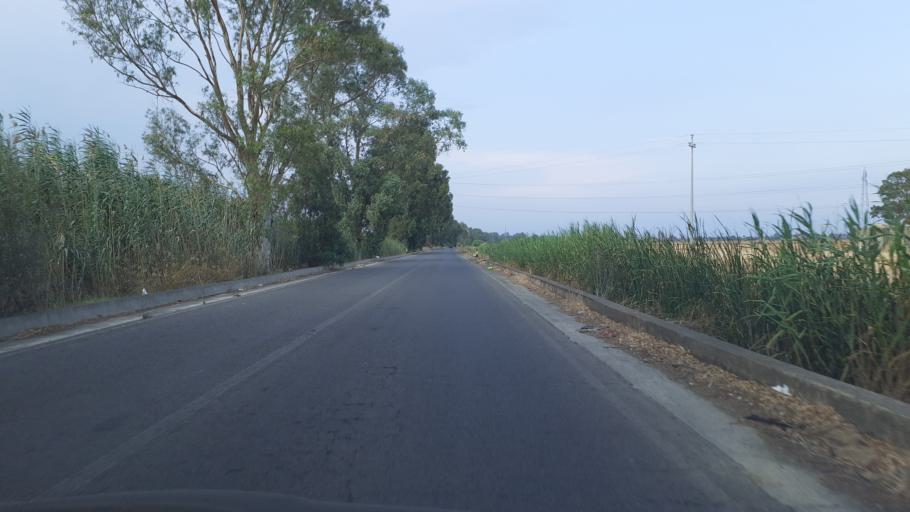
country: IT
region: Sicily
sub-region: Catania
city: Misterbianco
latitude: 37.4405
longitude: 15.0095
